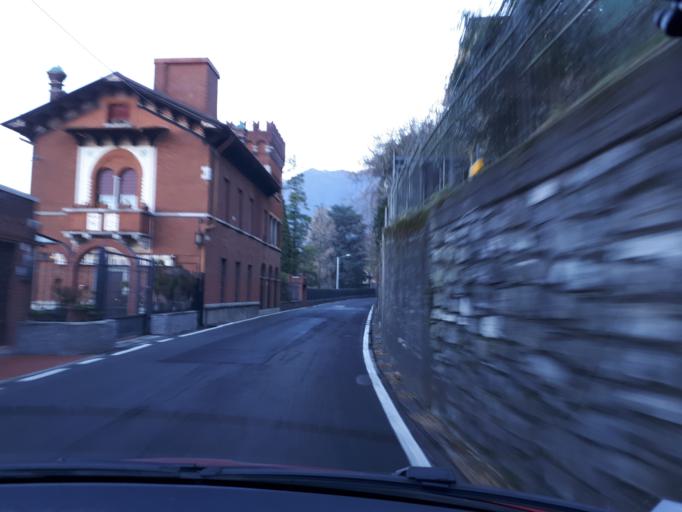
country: IT
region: Lombardy
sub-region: Provincia di Como
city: Brunate
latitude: 45.8255
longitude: 9.0817
